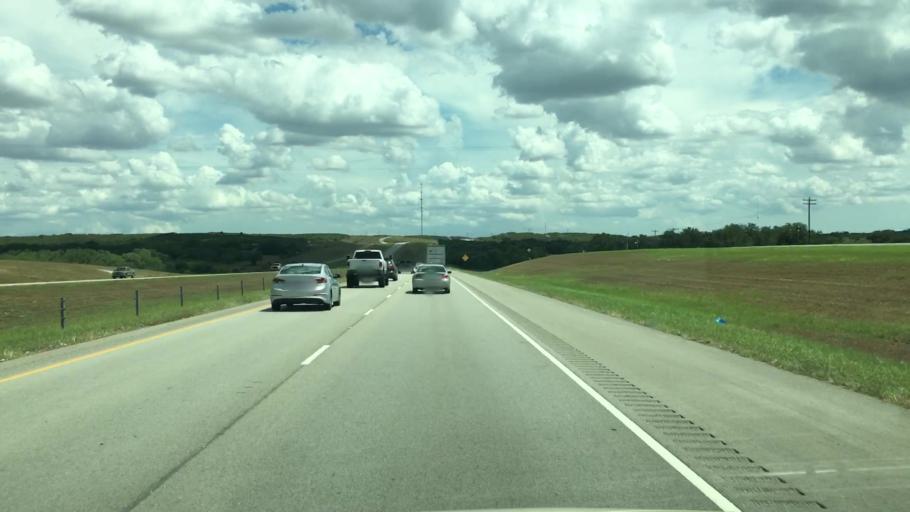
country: US
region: Texas
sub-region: Live Oak County
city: George West
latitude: 28.2644
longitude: -97.9350
